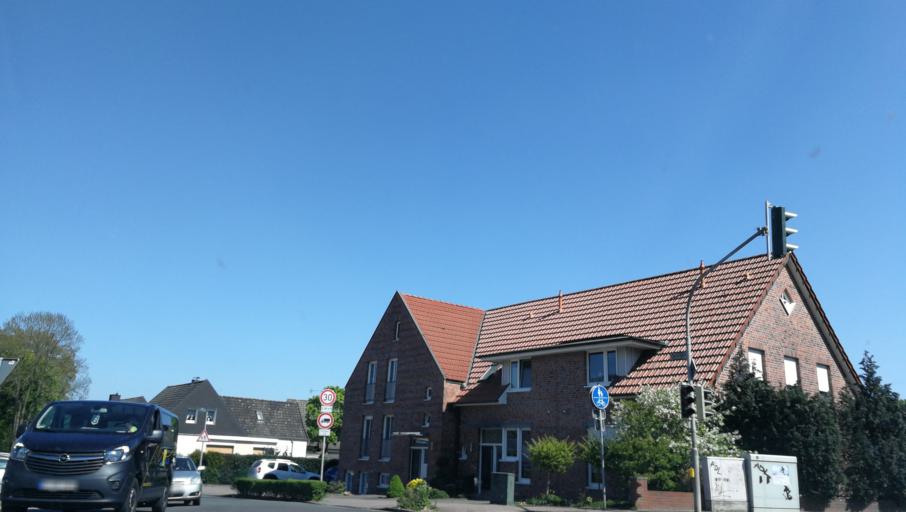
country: DE
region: North Rhine-Westphalia
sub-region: Regierungsbezirk Munster
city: Rheine
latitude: 52.2644
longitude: 7.4429
